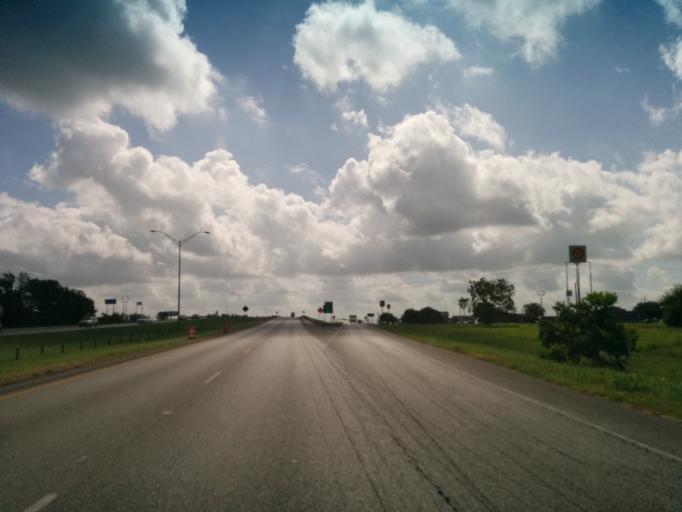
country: US
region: Texas
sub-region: Fayette County
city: Schulenburg
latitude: 29.6926
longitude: -96.9072
